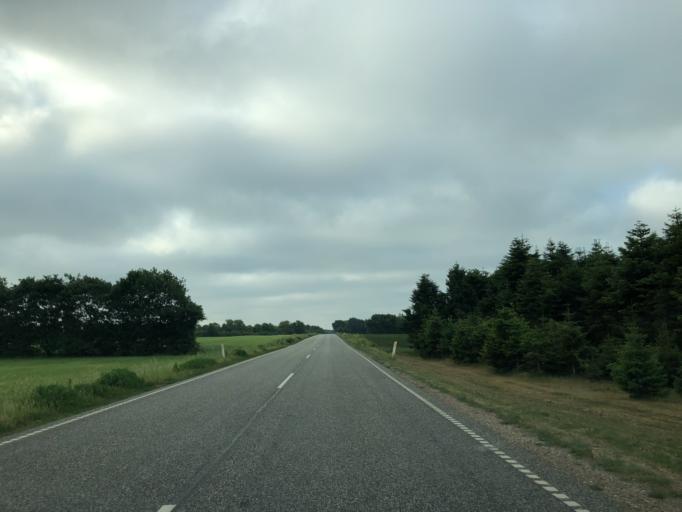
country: DK
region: South Denmark
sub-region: Vejle Kommune
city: Give
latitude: 55.8983
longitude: 9.2047
